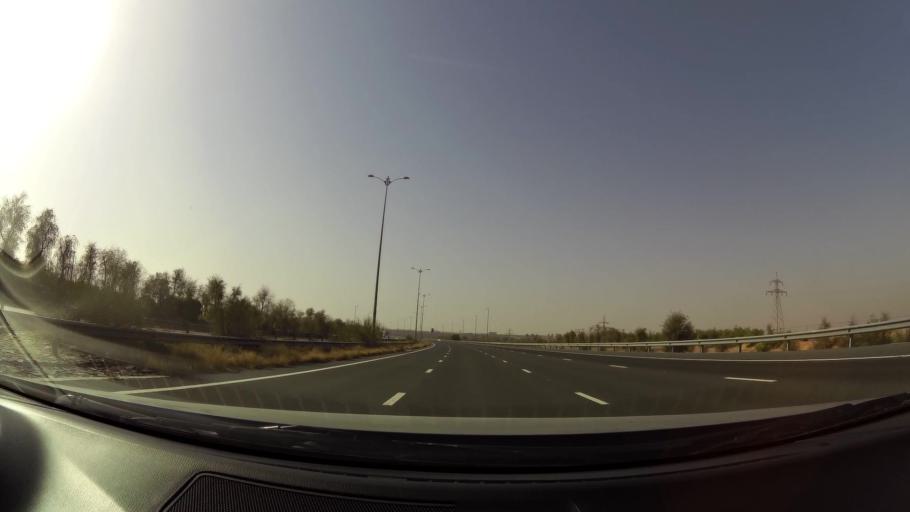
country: OM
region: Al Buraimi
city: Al Buraymi
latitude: 24.6465
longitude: 55.7051
